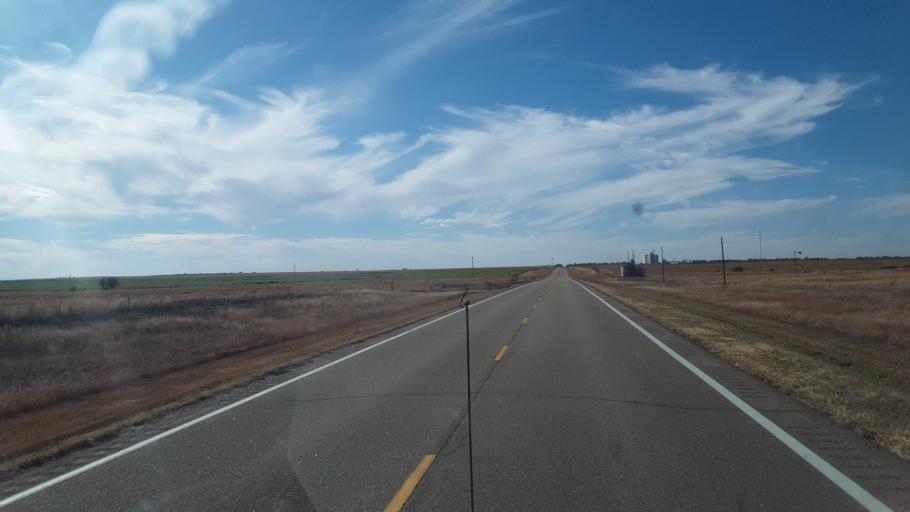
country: US
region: Kansas
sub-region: Edwards County
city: Kinsley
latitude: 38.1897
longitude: -99.4934
